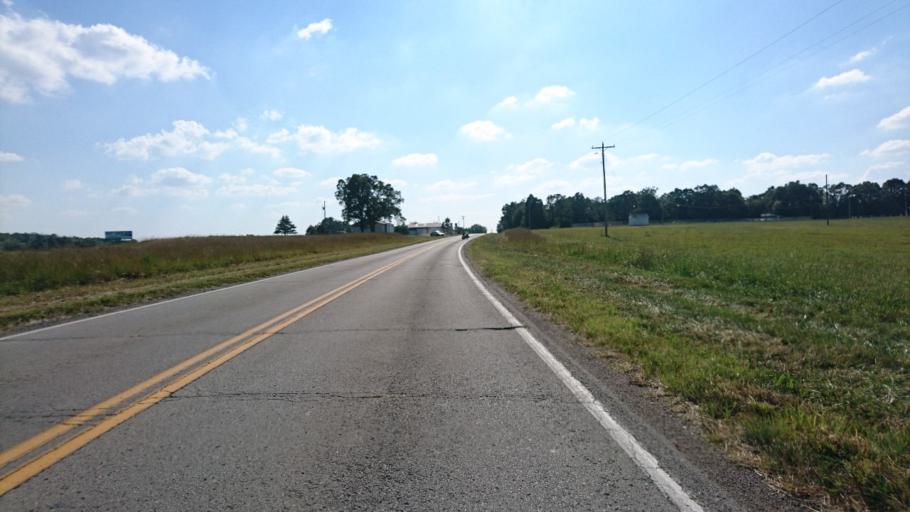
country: US
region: Missouri
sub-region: Laclede County
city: Lebanon
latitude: 37.6402
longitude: -92.6756
